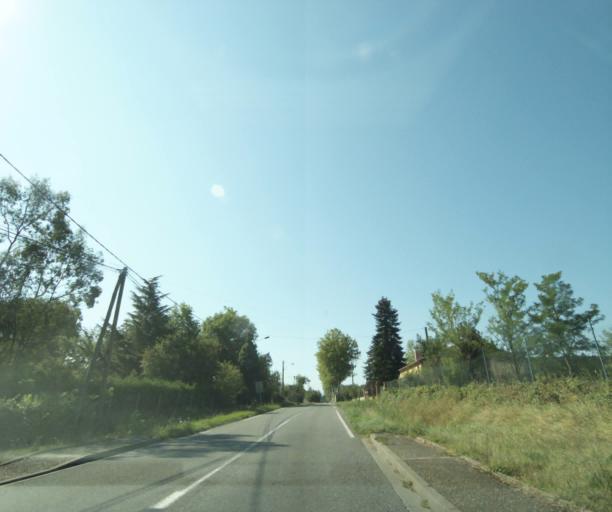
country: FR
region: Midi-Pyrenees
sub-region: Departement de la Haute-Garonne
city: Saint-Sulpice-sur-Leze
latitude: 43.3239
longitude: 1.3225
